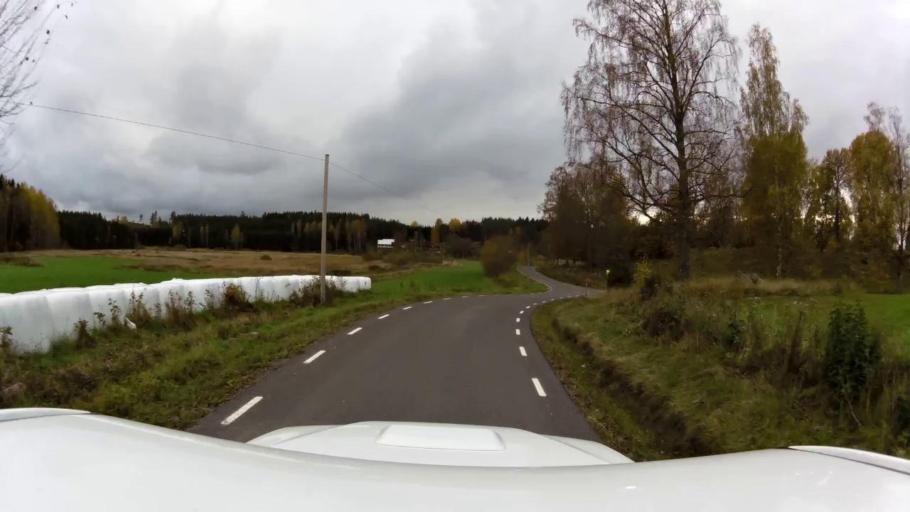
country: SE
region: OEstergoetland
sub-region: Linkopings Kommun
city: Ljungsbro
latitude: 58.5715
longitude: 15.4612
